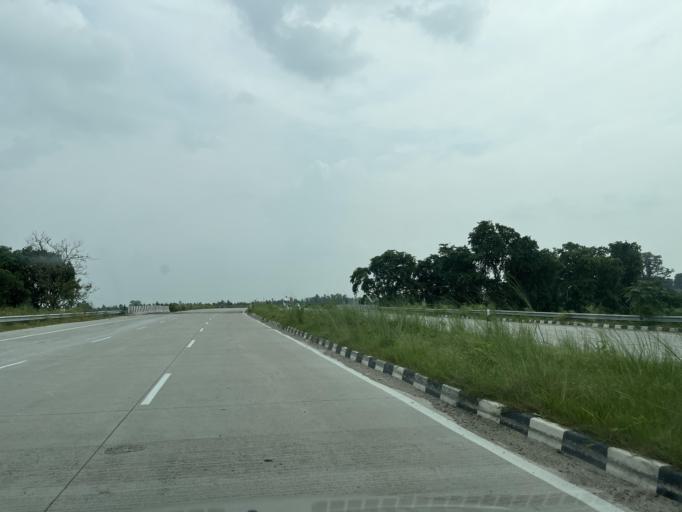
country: IN
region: Uttarakhand
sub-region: Udham Singh Nagar
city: Kashipur
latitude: 29.1902
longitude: 78.9389
